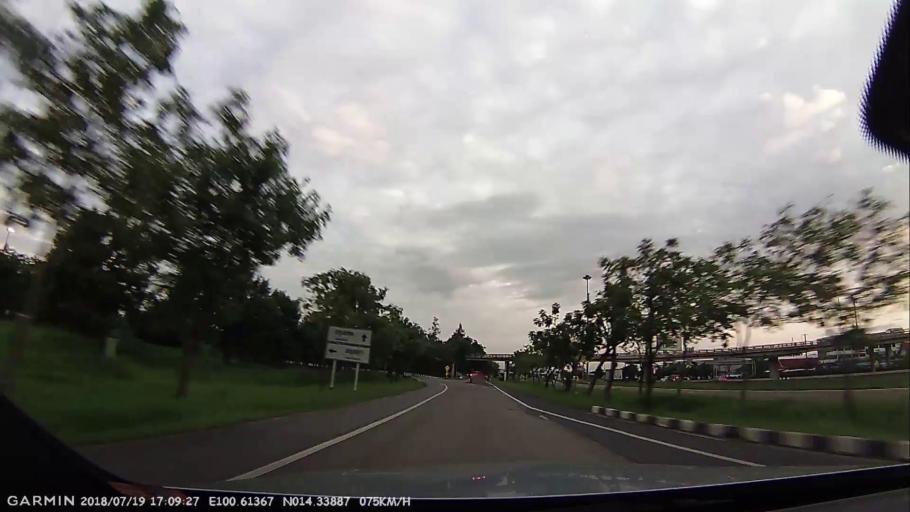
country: TH
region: Phra Nakhon Si Ayutthaya
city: Phra Nakhon Si Ayutthaya
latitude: 14.3388
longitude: 100.6137
